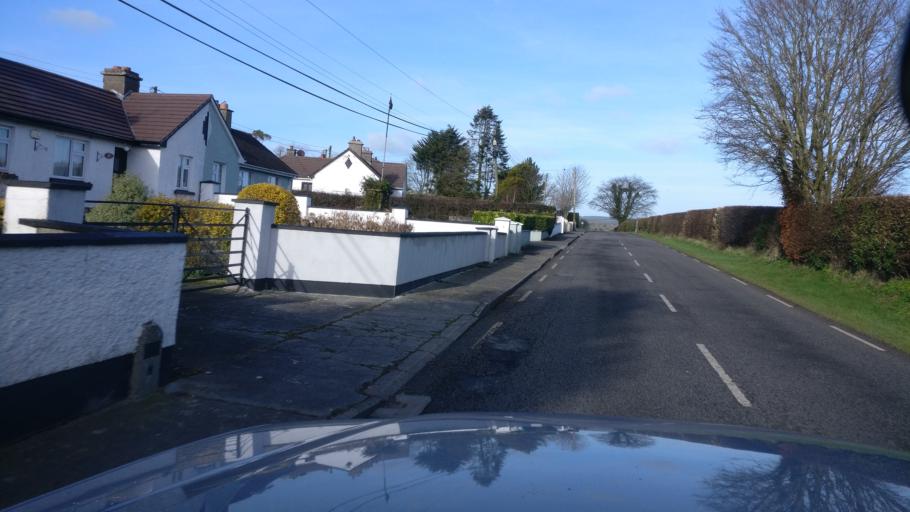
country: IE
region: Leinster
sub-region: Kilkenny
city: Castlecomer
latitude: 52.8701
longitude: -7.1644
